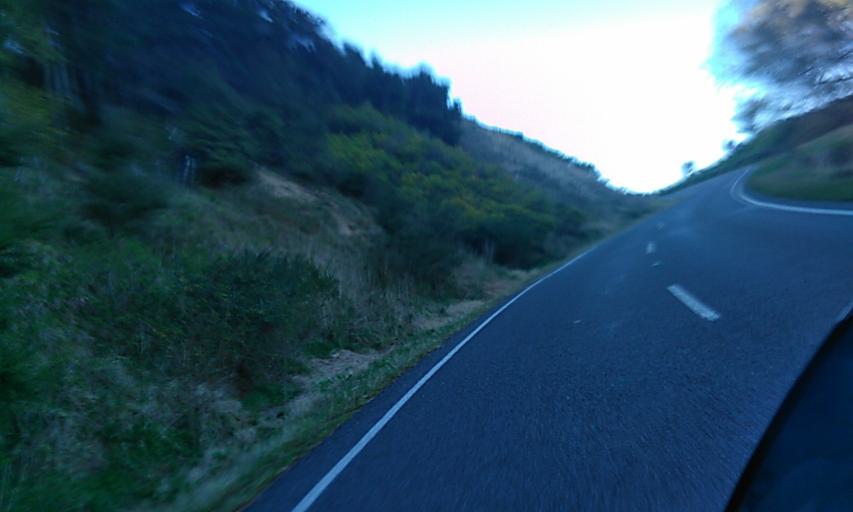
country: NZ
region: Gisborne
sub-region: Gisborne District
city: Gisborne
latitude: -38.5928
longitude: 177.9756
